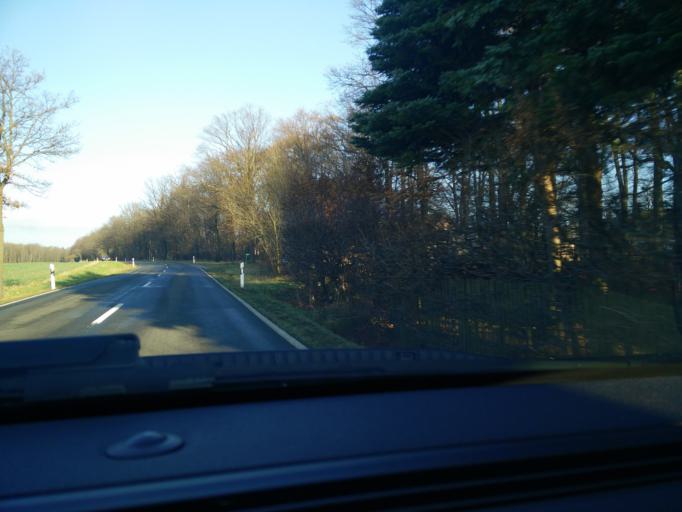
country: DE
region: Saxony
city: Geithain
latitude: 51.0703
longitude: 12.7180
